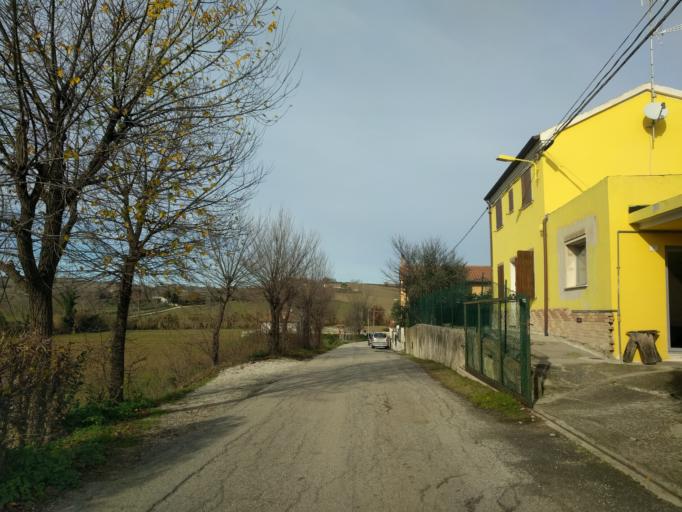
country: IT
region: The Marches
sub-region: Provincia di Pesaro e Urbino
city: Cuccurano
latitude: 43.7982
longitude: 12.9477
